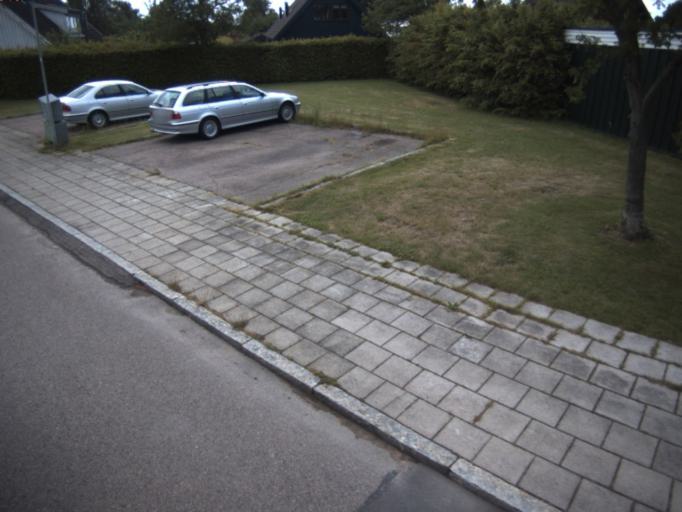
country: SE
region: Skane
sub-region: Helsingborg
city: Helsingborg
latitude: 56.0281
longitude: 12.7510
